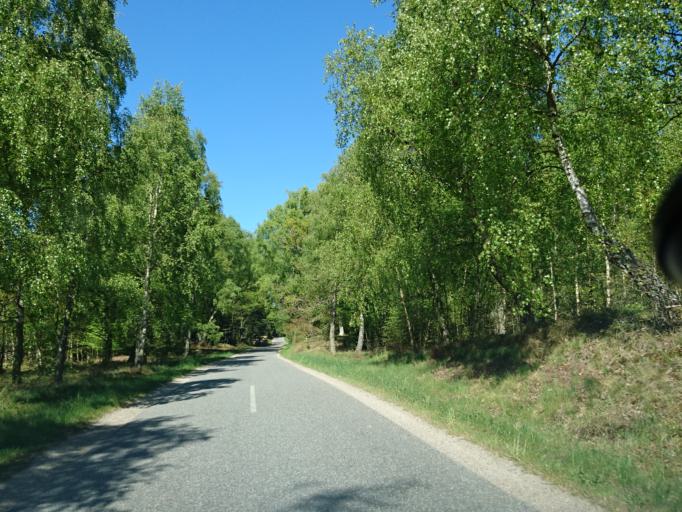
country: DK
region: North Denmark
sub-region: Hjorring Kommune
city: Sindal
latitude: 57.5923
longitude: 10.2301
